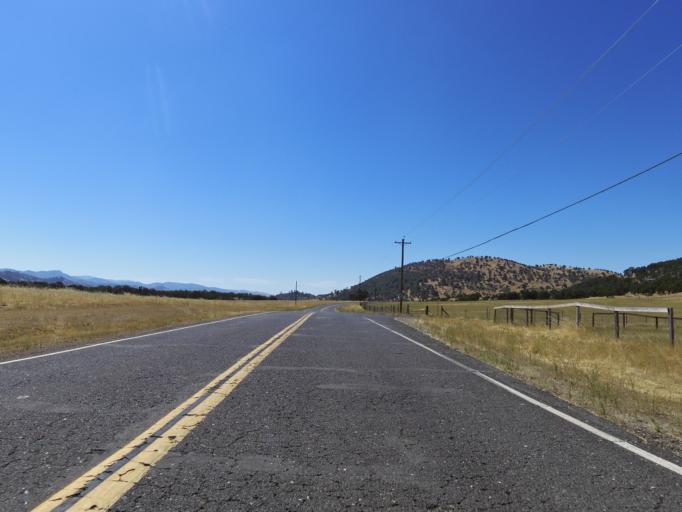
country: US
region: California
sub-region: Tuolumne County
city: Tuolumne City
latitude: 37.6421
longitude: -120.3091
